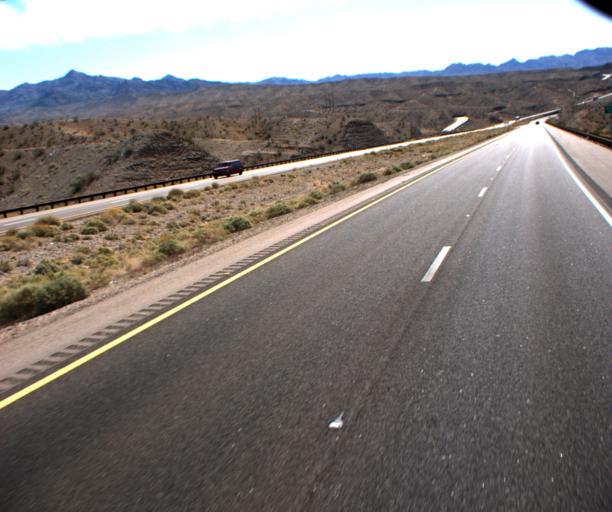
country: US
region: Nevada
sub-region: Clark County
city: Boulder City
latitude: 35.9828
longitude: -114.7056
